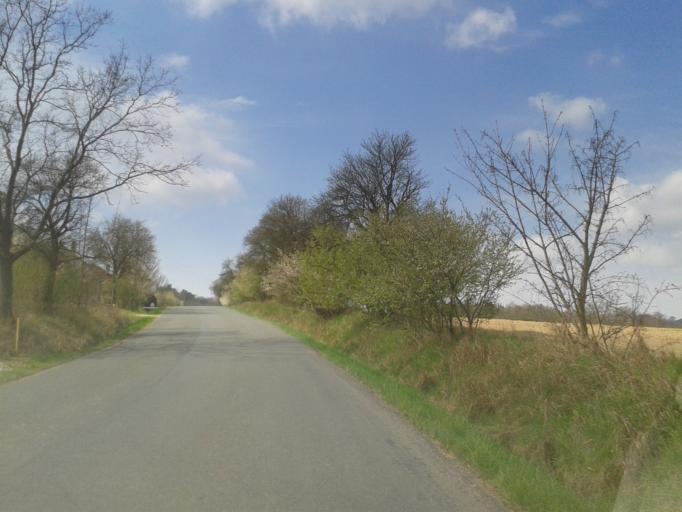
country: CZ
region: Central Bohemia
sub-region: Okres Beroun
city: Lodenice
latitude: 50.0109
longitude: 14.1383
